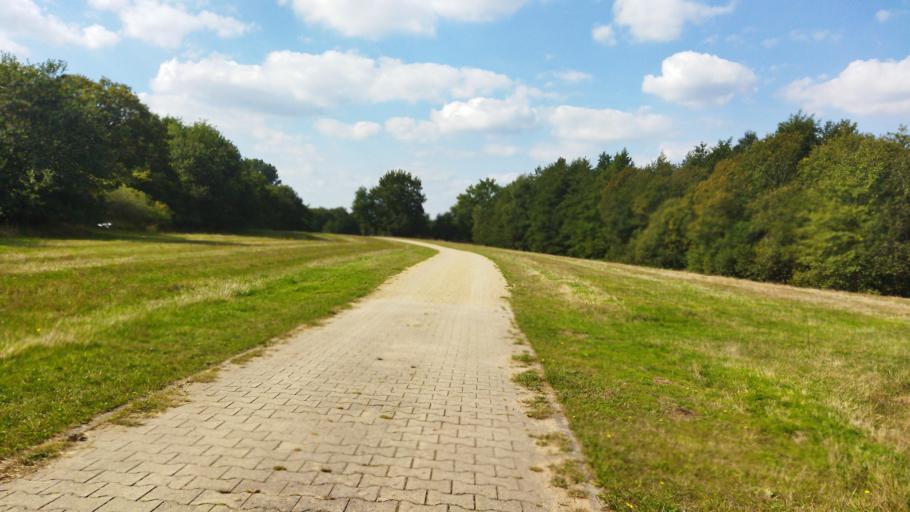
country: DE
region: Lower Saxony
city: Haren
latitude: 52.7826
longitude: 7.2583
